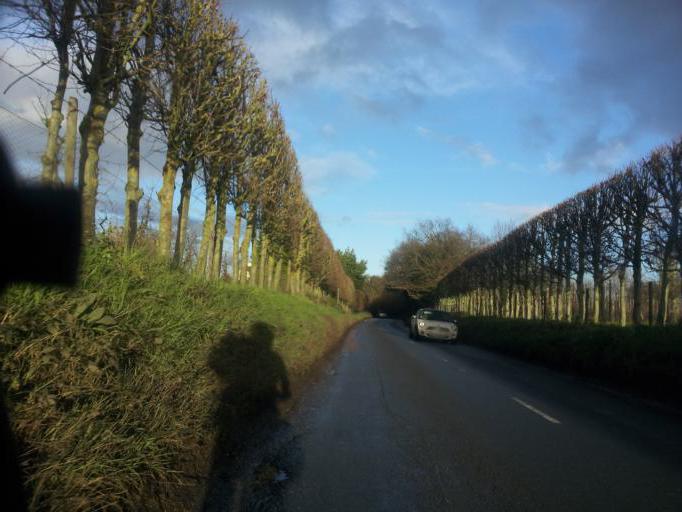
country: GB
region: England
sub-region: Kent
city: Meopham
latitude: 51.3909
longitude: 0.3887
